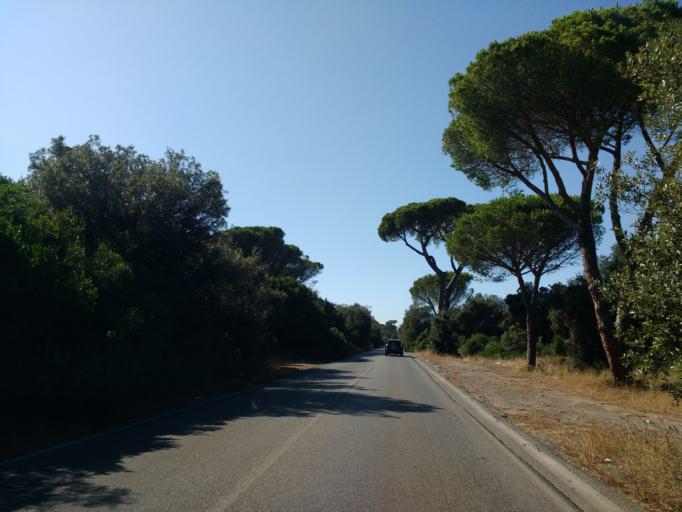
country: IT
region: Latium
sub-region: Citta metropolitana di Roma Capitale
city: Acilia-Castel Fusano-Ostia Antica
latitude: 41.7166
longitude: 12.3528
